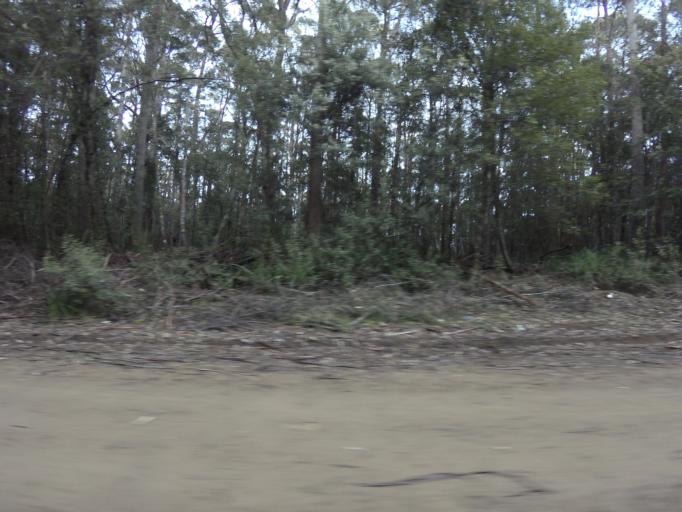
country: AU
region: Tasmania
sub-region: Huon Valley
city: Geeveston
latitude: -43.4982
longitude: 146.8788
